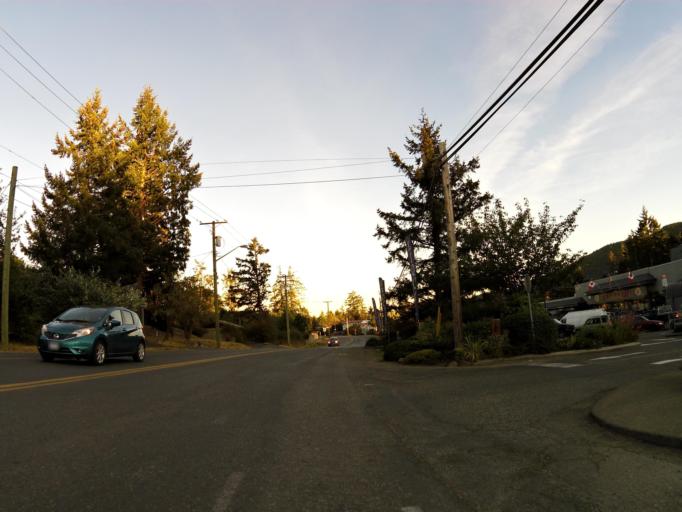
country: CA
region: British Columbia
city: North Cowichan
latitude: 48.8613
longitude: -123.5115
